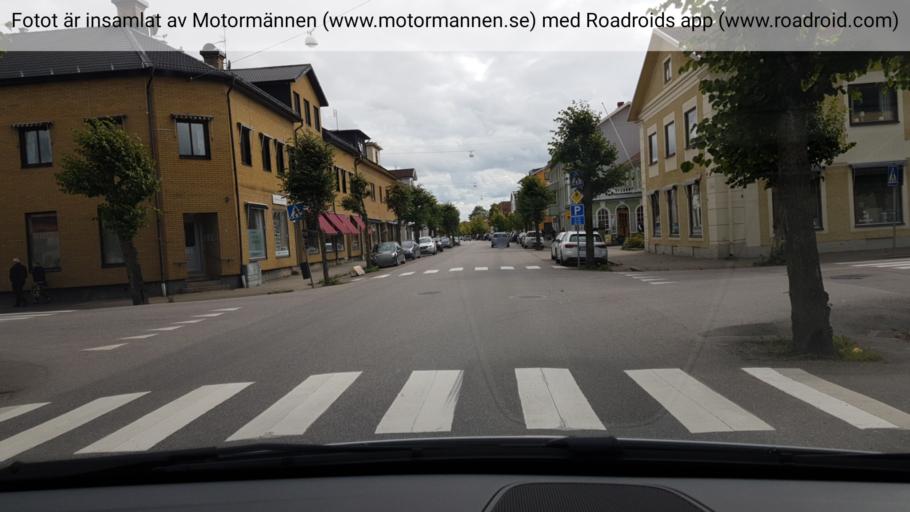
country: SE
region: Vaestra Goetaland
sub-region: Vara Kommun
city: Vara
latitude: 58.2613
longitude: 12.9529
